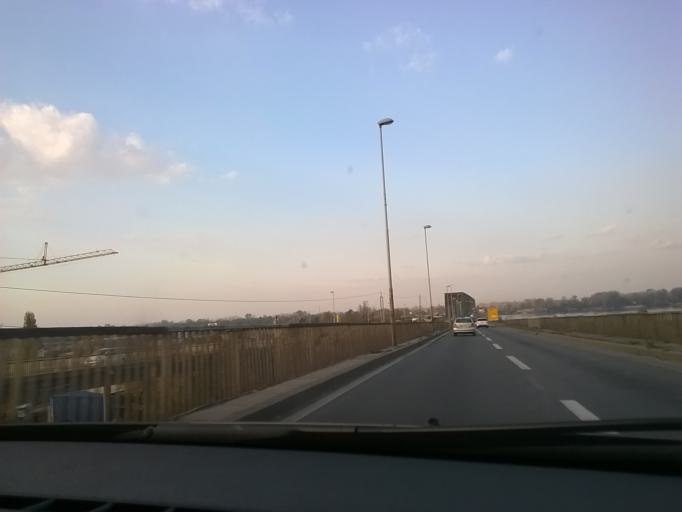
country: RS
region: Central Serbia
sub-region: Belgrade
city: Palilula
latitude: 44.8215
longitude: 20.4909
